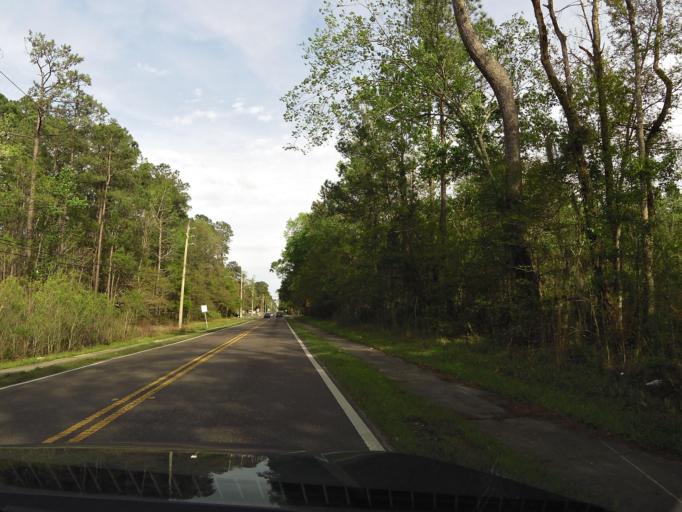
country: US
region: Florida
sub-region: Clay County
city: Bellair-Meadowbrook Terrace
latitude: 30.2262
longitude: -81.7495
